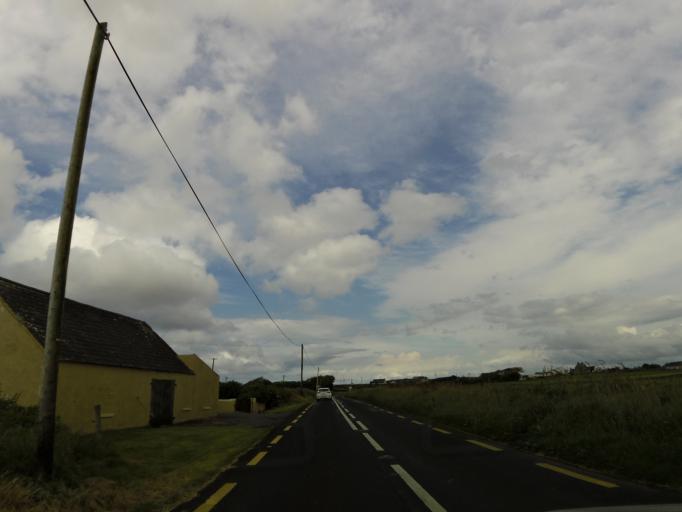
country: IE
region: Munster
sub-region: An Clar
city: Kilrush
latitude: 52.7196
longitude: -9.5870
